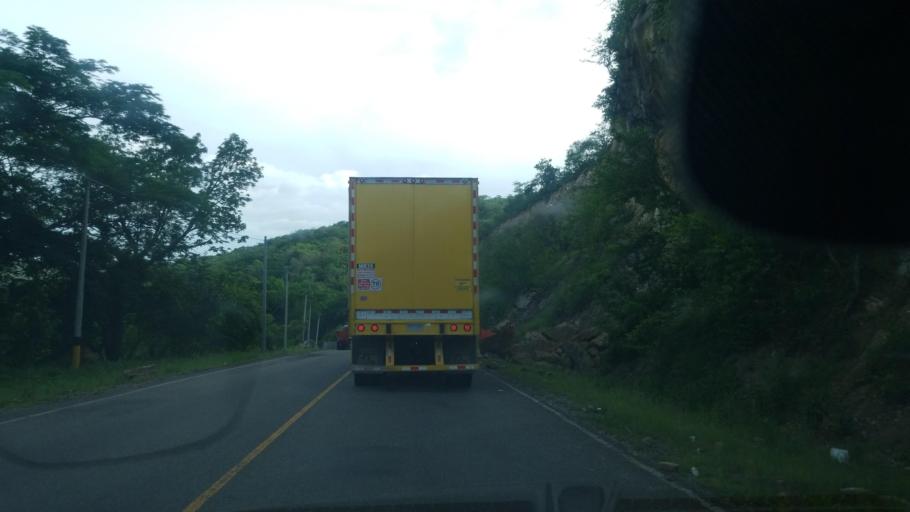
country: HN
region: Santa Barbara
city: Ilama
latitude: 15.0775
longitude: -88.2246
